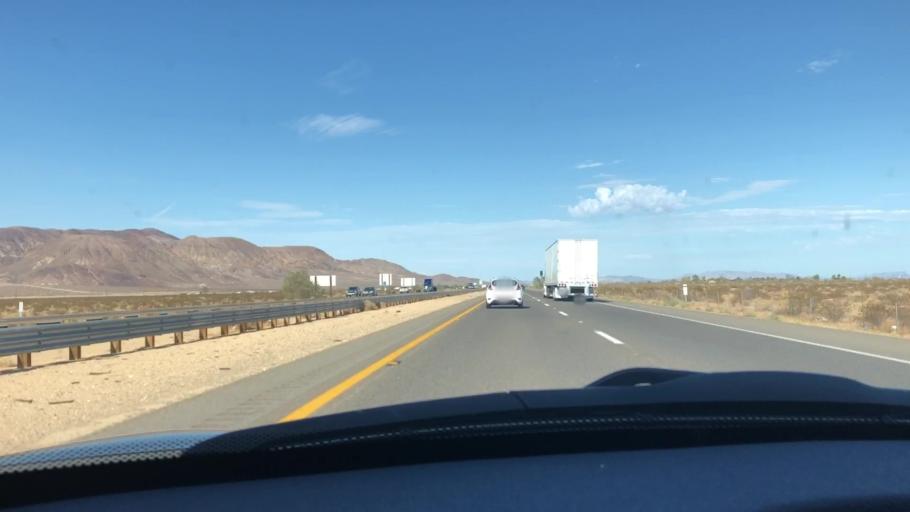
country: US
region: California
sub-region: San Bernardino County
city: Barstow
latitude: 34.9037
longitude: -116.8779
